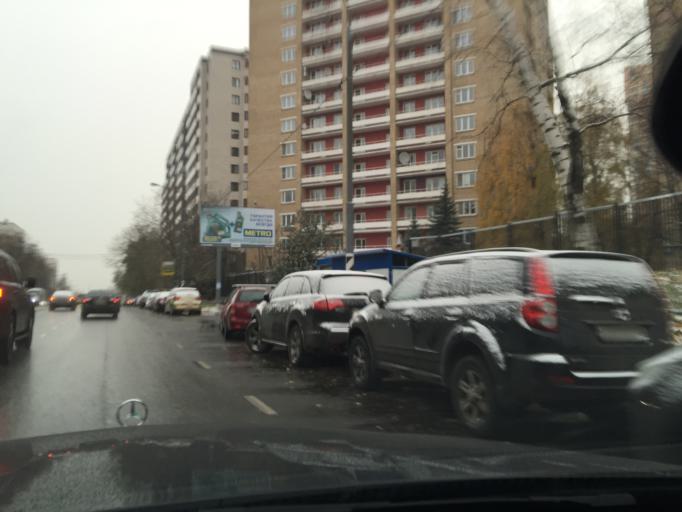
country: RU
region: Moskovskaya
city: Semenovskoye
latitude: 55.6785
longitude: 37.5442
